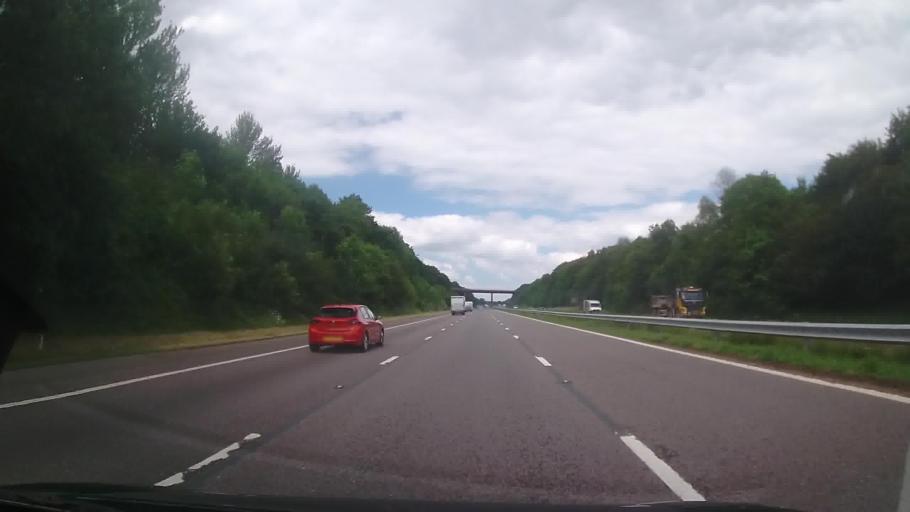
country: GB
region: England
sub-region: Devon
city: Cullompton
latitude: 50.8770
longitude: -3.3814
